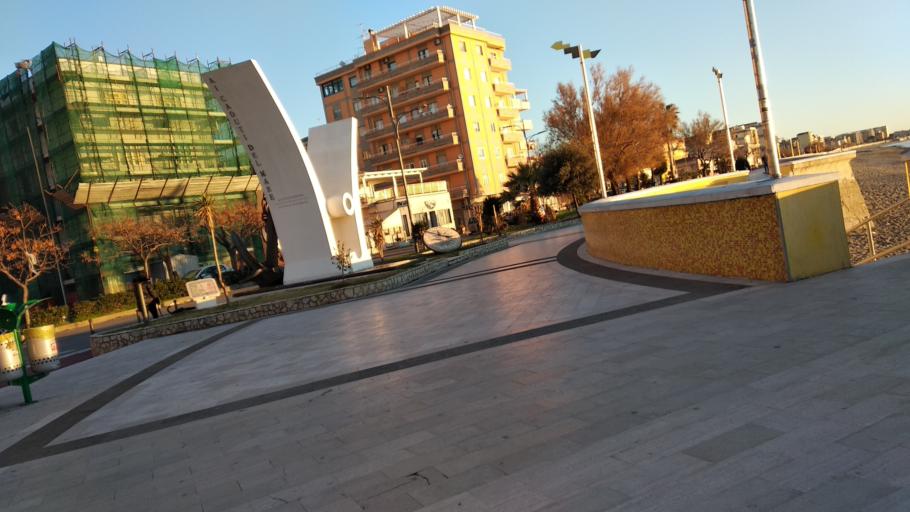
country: IT
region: Calabria
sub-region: Provincia di Catanzaro
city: Roccelletta
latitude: 38.8190
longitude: 16.6135
